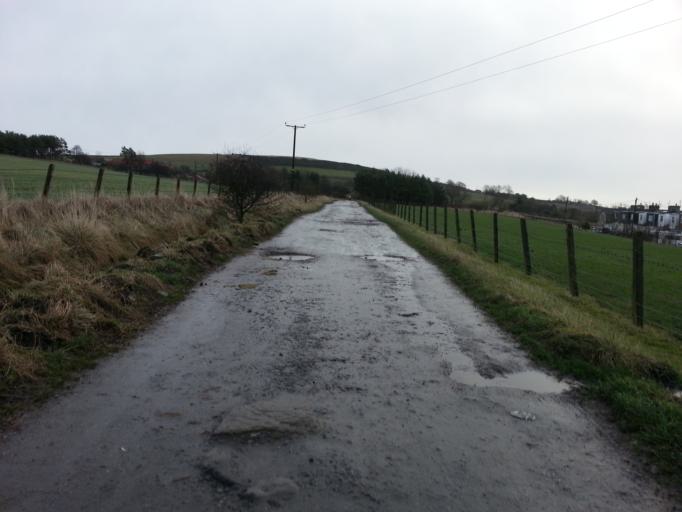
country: GB
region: England
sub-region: County Durham
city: Crook
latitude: 54.7265
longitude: -1.7483
